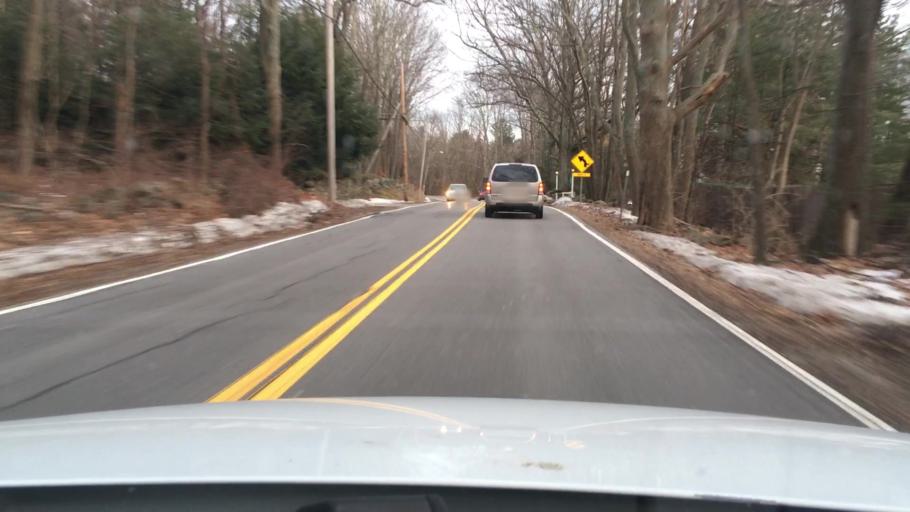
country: US
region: New Hampshire
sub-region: Rockingham County
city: Atkinson
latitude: 42.8262
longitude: -71.1355
